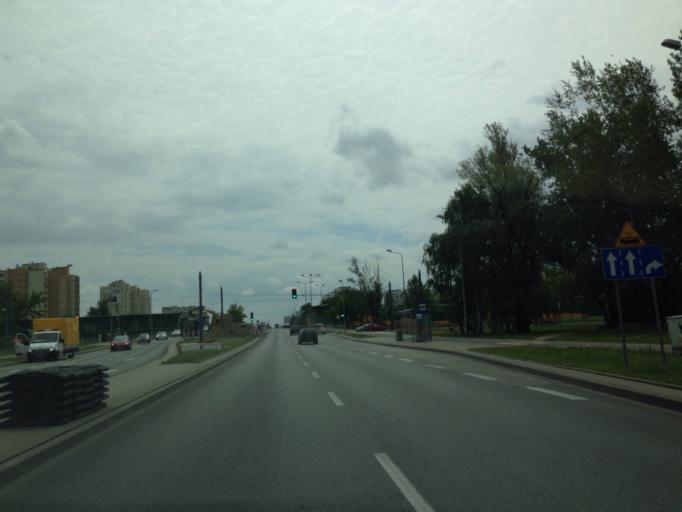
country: PL
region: Masovian Voivodeship
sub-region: Warszawa
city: Bemowo
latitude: 52.2476
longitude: 20.9113
